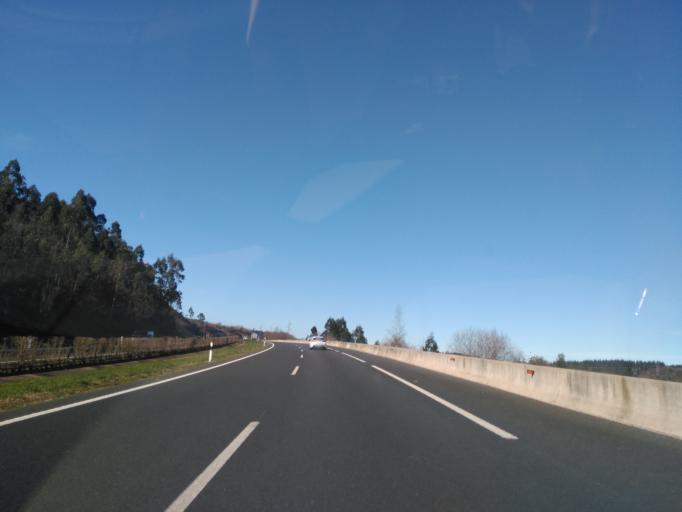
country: ES
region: Cantabria
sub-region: Provincia de Cantabria
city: Cabezon de la Sal
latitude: 43.3211
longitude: -4.2718
